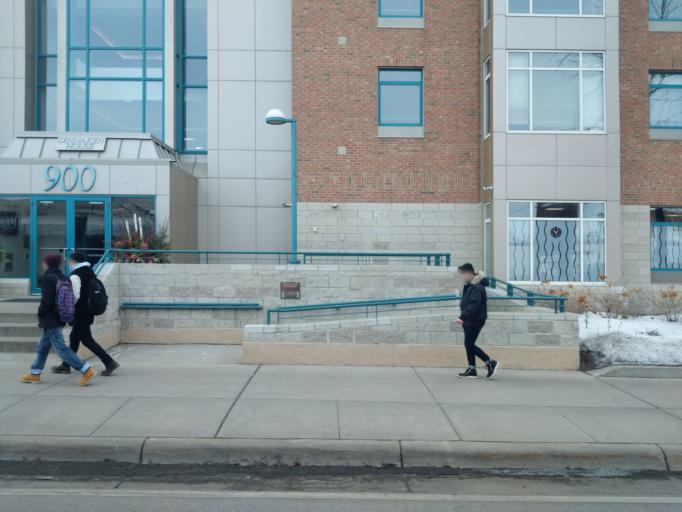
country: US
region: Minnesota
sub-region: Ramsey County
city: Lauderdale
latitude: 44.9735
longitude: -93.2248
